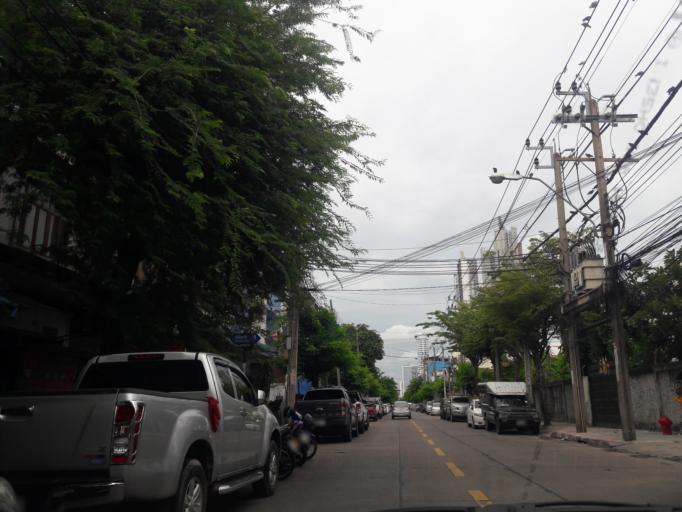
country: TH
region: Bangkok
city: Khlong San
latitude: 13.7269
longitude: 100.5017
